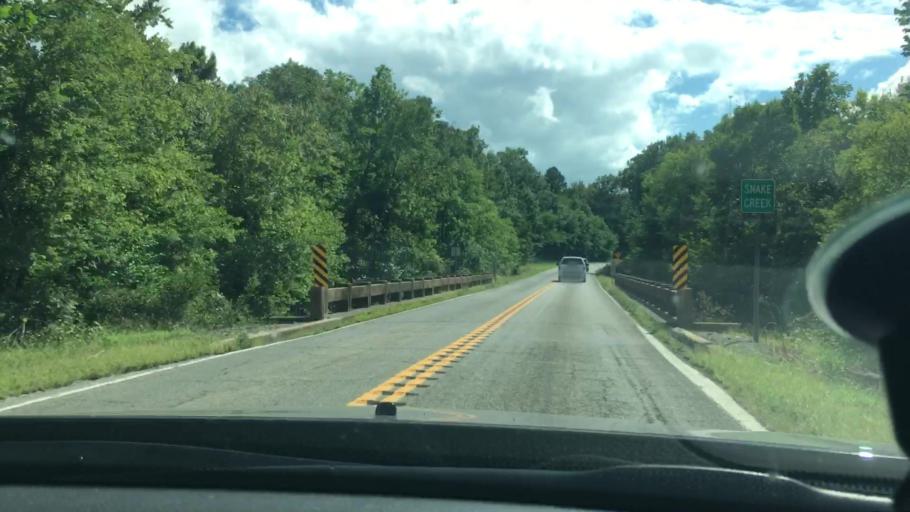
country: US
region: Oklahoma
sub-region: Sequoyah County
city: Vian
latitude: 35.6382
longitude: -94.9607
